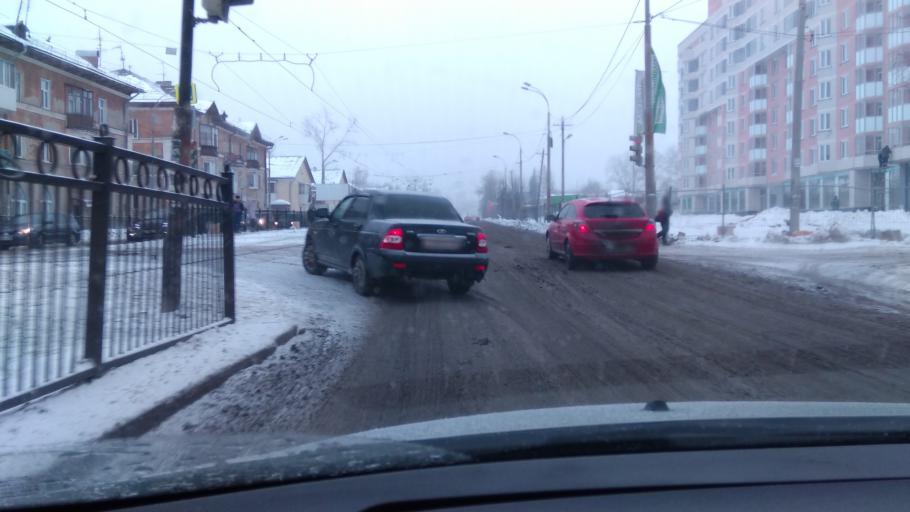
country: RU
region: Sverdlovsk
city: Yekaterinburg
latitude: 56.9020
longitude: 60.5834
